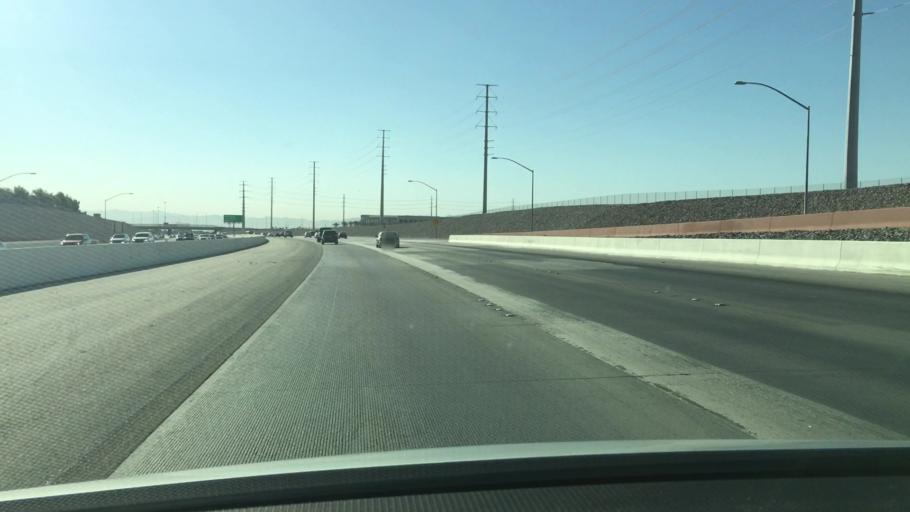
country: US
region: Nevada
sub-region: Clark County
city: Summerlin South
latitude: 36.1205
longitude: -115.3241
